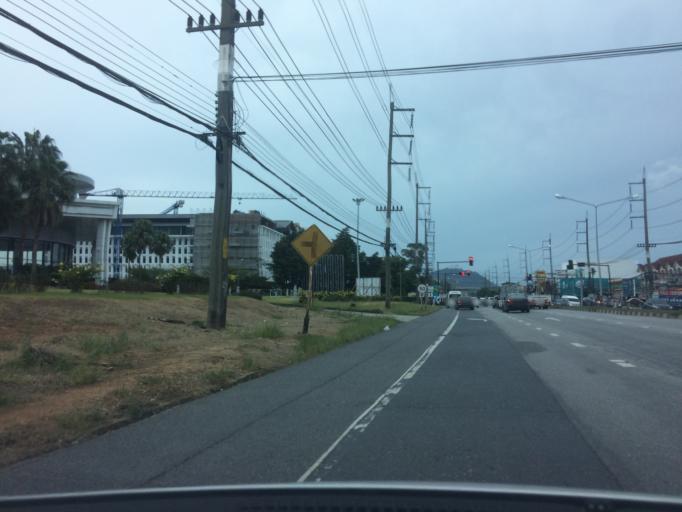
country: TH
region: Phuket
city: Mueang Phuket
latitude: 7.8682
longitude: 98.3563
